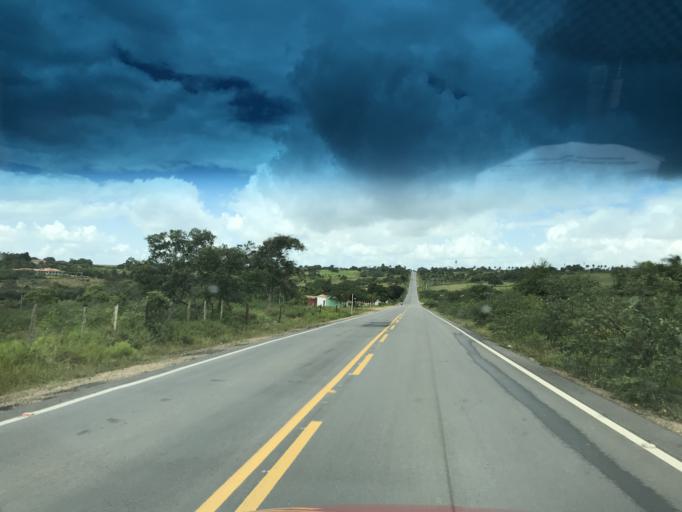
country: BR
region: Bahia
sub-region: Conceicao Do Almeida
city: Conceicao do Almeida
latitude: -12.6857
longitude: -39.2518
